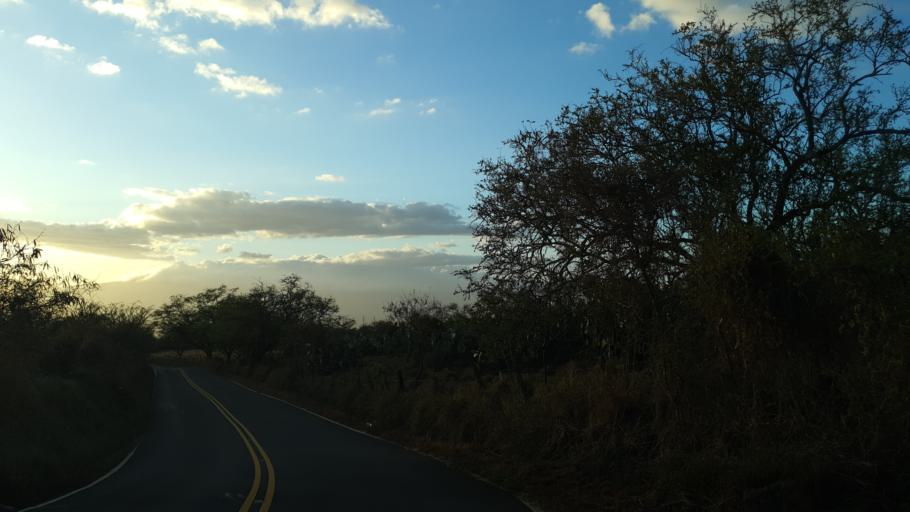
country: US
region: Hawaii
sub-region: Maui County
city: Pukalani
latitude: 20.7837
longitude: -156.3453
